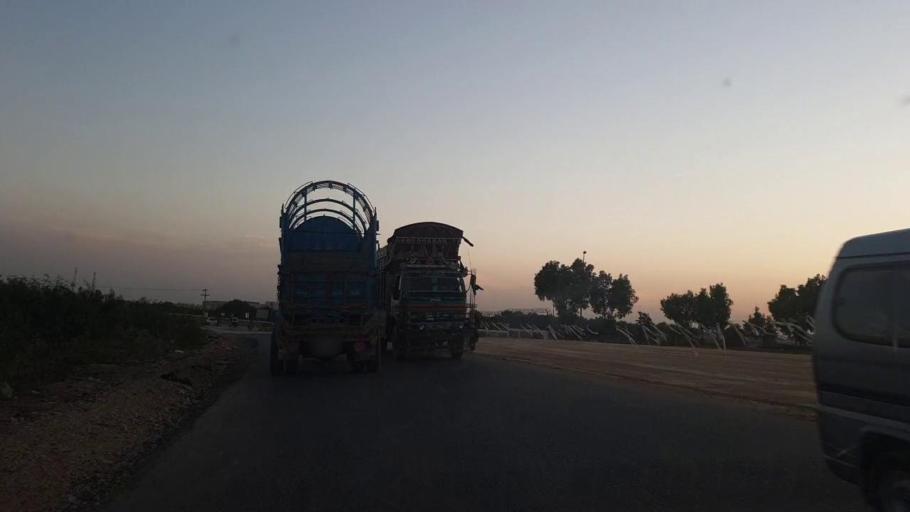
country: PK
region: Sindh
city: Jamshoro
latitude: 25.4081
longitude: 68.2672
